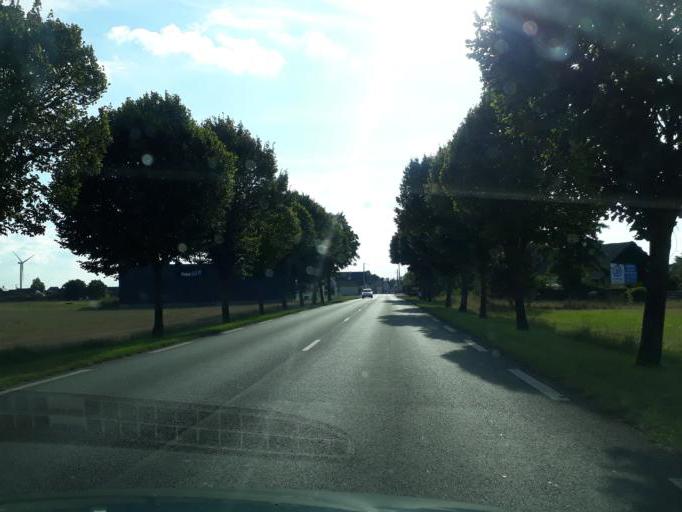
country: FR
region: Centre
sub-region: Departement du Loir-et-Cher
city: Ouzouer-le-Marche
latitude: 47.9041
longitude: 1.4697
